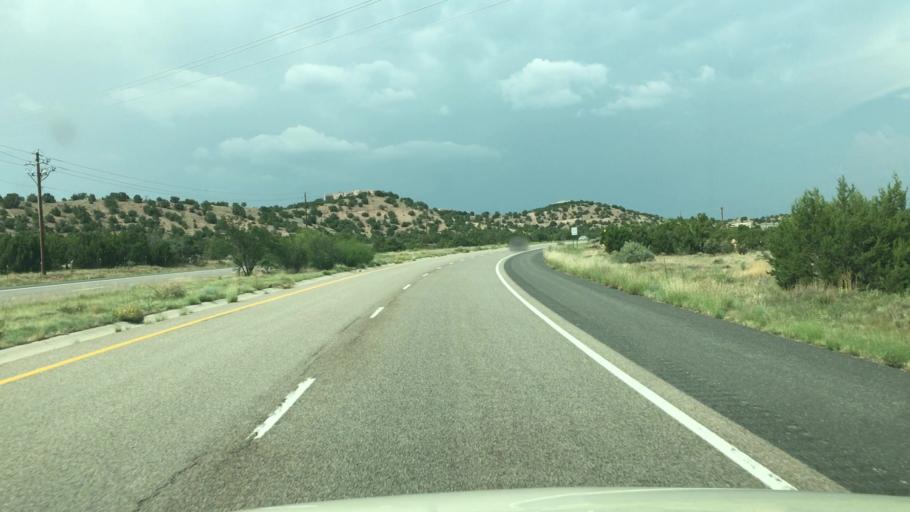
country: US
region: New Mexico
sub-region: Santa Fe County
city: Eldorado at Santa Fe
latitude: 35.4813
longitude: -105.9082
